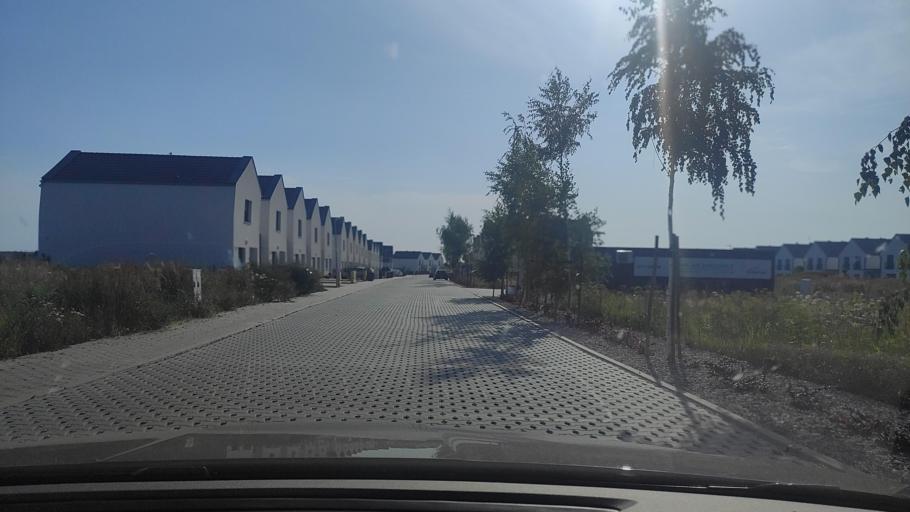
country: PL
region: Greater Poland Voivodeship
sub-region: Powiat poznanski
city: Kostrzyn
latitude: 52.4085
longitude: 17.2175
